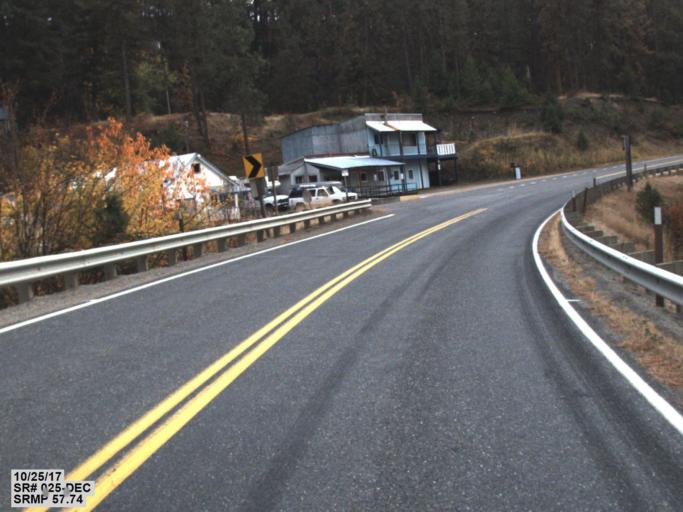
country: US
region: Washington
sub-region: Stevens County
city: Kettle Falls
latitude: 48.3071
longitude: -118.1468
